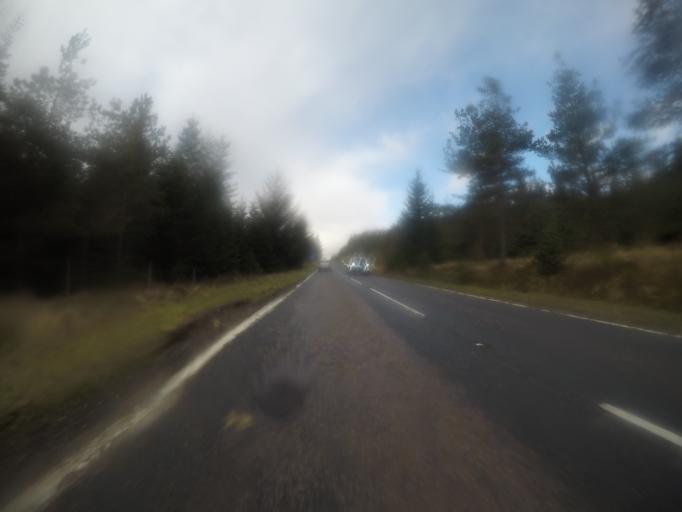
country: GB
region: Scotland
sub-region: Highland
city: Spean Bridge
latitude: 57.0819
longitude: -4.9441
